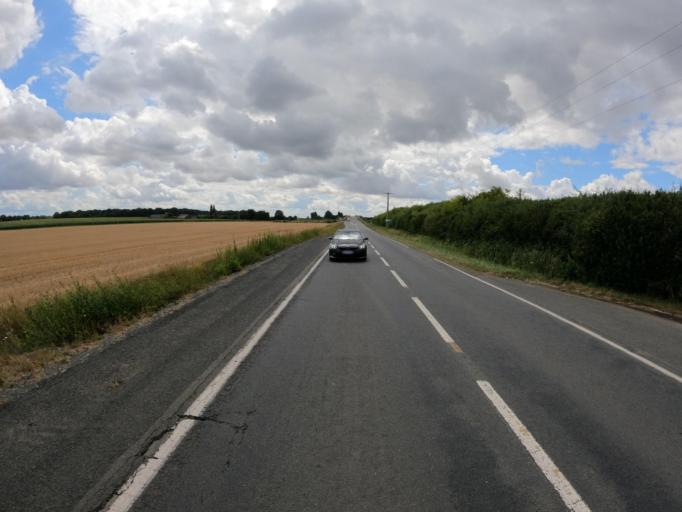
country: FR
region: Pays de la Loire
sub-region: Departement de la Sarthe
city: Juigne-sur-Sarthe
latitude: 47.8745
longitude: -0.3056
